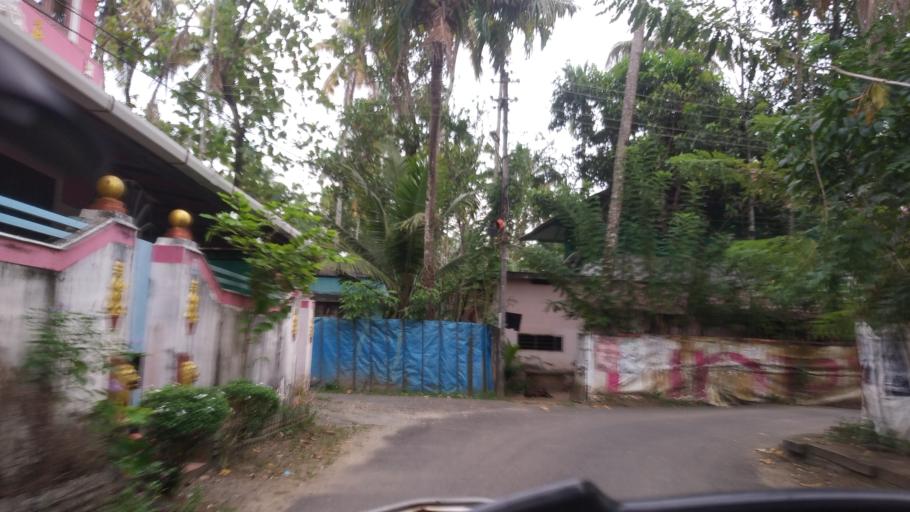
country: IN
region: Kerala
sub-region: Thrissur District
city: Kodungallur
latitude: 10.1368
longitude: 76.2000
